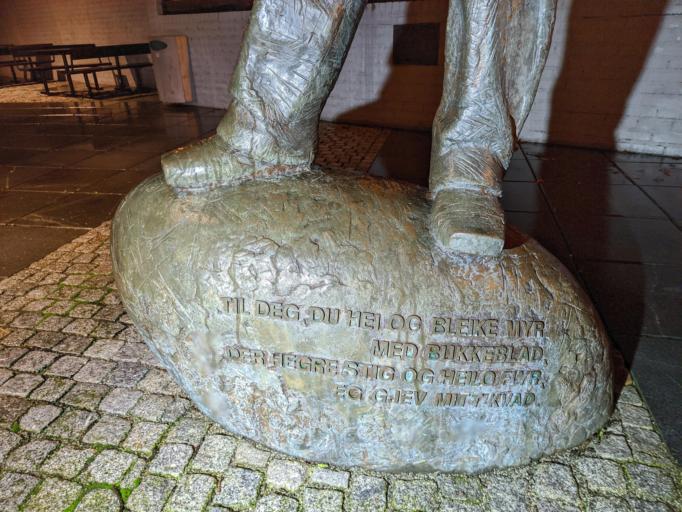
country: NO
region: Rogaland
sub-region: Time
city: Bryne
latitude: 58.7359
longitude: 5.6477
